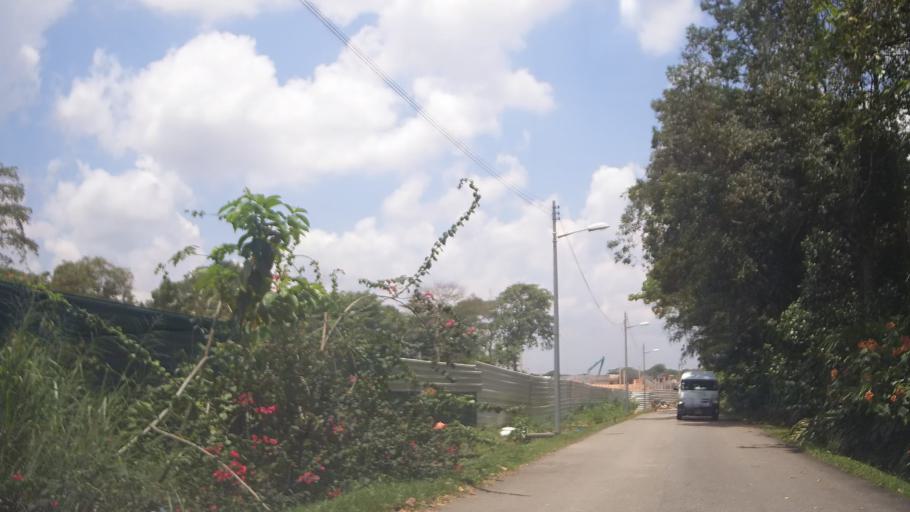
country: MY
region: Johor
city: Kampung Pasir Gudang Baru
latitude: 1.3920
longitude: 103.8677
